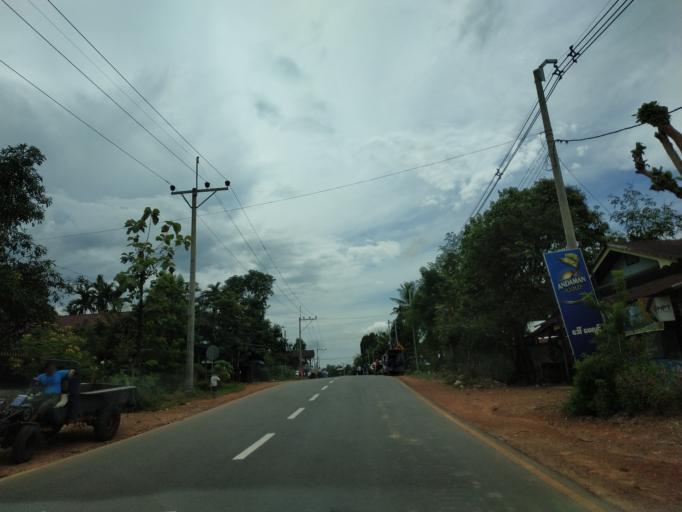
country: MM
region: Tanintharyi
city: Dawei
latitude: 14.0434
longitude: 98.2210
